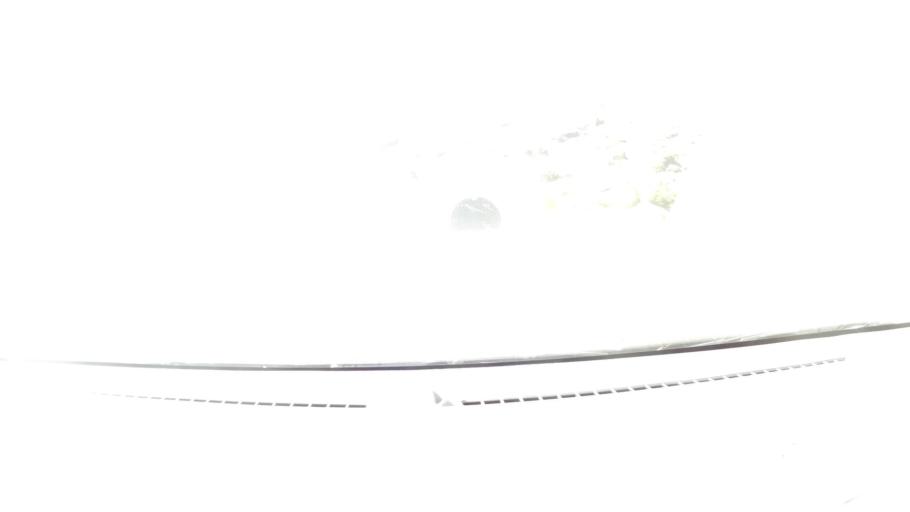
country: CL
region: Valparaiso
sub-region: Provincia de Valparaiso
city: Valparaiso
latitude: -33.0424
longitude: -71.6536
